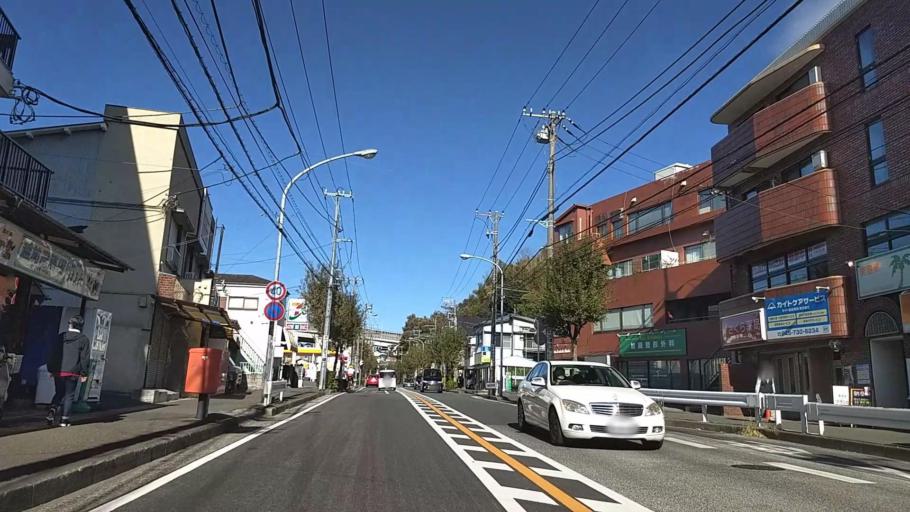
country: JP
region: Kanagawa
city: Yokohama
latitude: 35.4240
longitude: 139.5846
